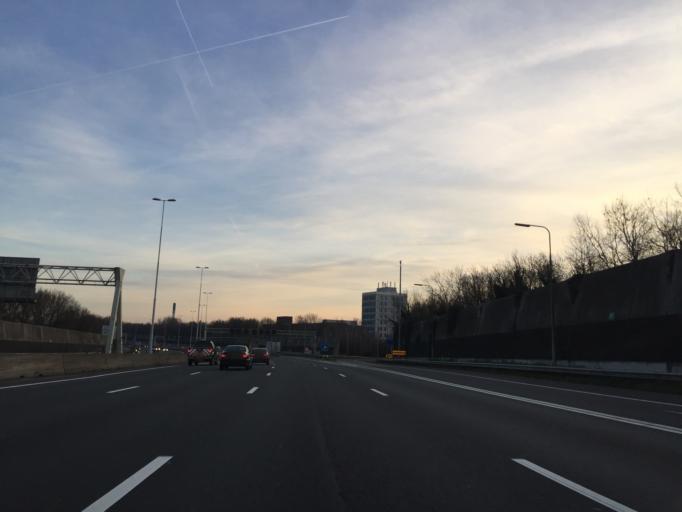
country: NL
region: South Holland
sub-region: Gemeente Zwijndrecht
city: Zwijndrecht
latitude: 51.8183
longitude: 4.6290
